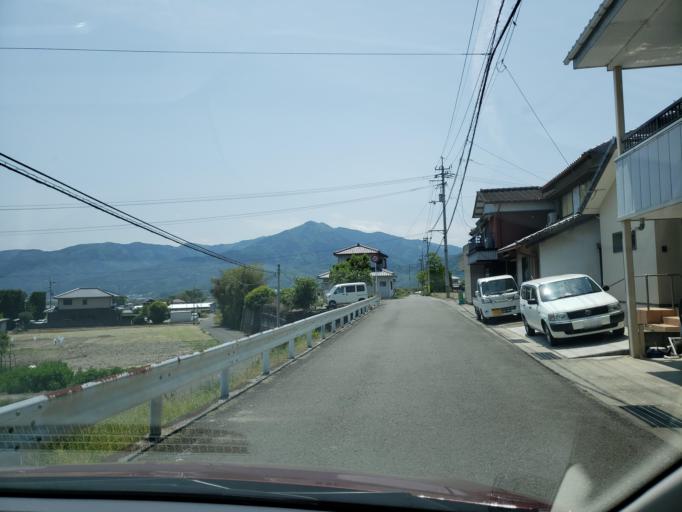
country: JP
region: Tokushima
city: Wakimachi
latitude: 34.0907
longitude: 134.2199
